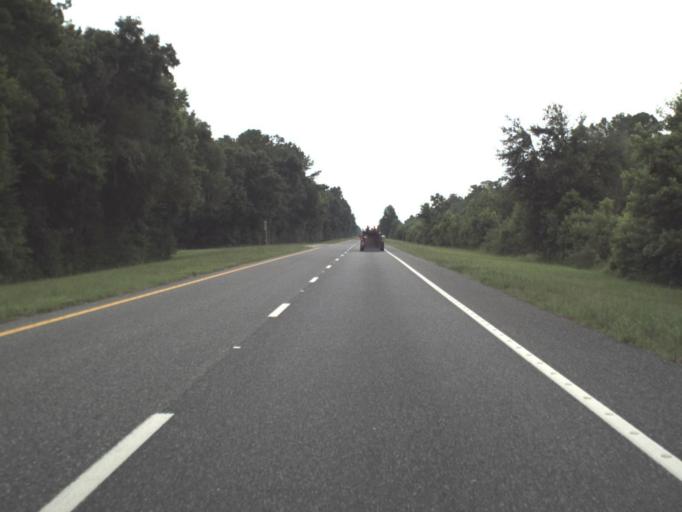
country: US
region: Florida
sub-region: Levy County
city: Williston Highlands
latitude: 29.2637
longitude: -82.7295
